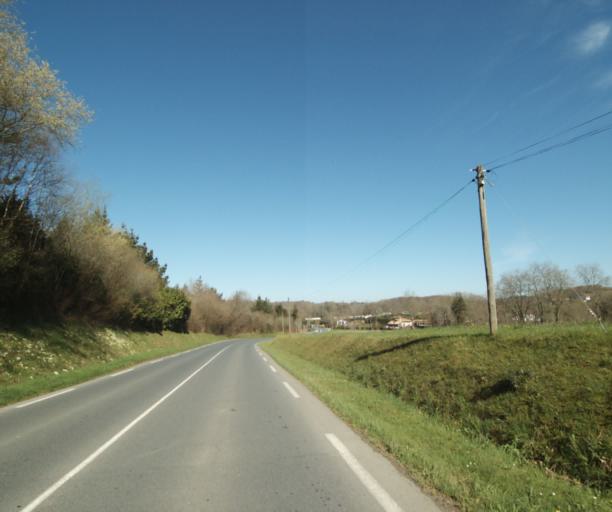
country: FR
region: Aquitaine
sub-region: Departement des Pyrenees-Atlantiques
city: Urrugne
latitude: 43.3577
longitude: -1.6918
